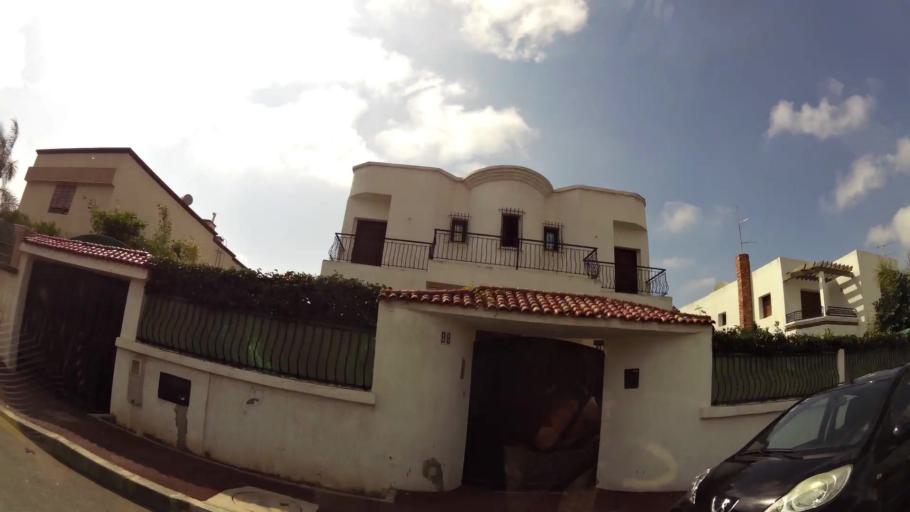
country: MA
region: Rabat-Sale-Zemmour-Zaer
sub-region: Skhirate-Temara
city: Temara
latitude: 33.9620
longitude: -6.8718
